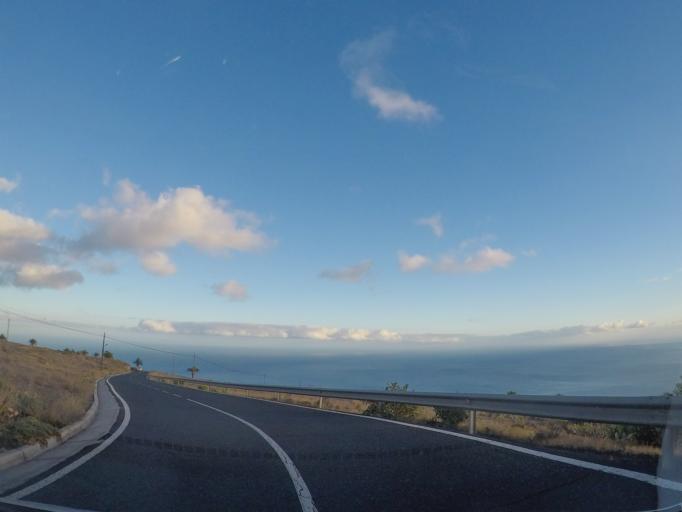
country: ES
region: Canary Islands
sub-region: Provincia de Santa Cruz de Tenerife
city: Alajero
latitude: 28.0488
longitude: -17.2330
